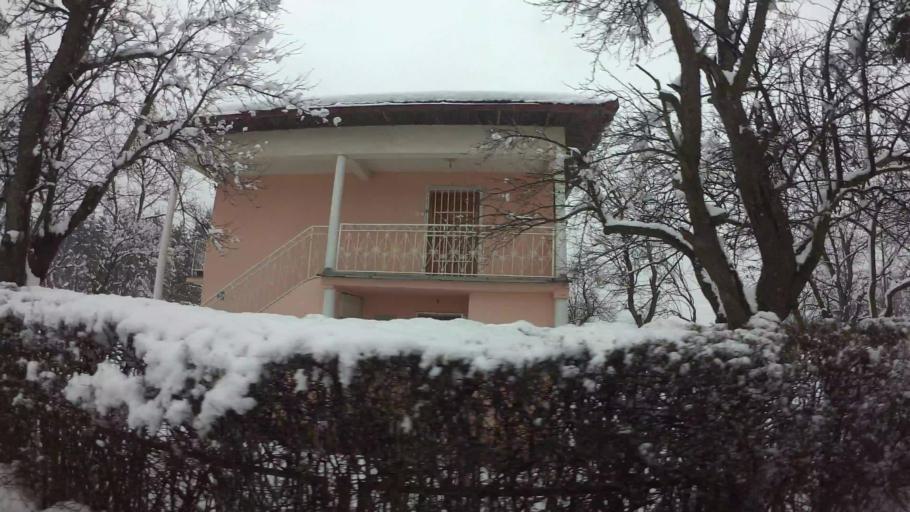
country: BA
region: Federation of Bosnia and Herzegovina
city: Hadzici
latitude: 43.8505
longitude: 18.2588
